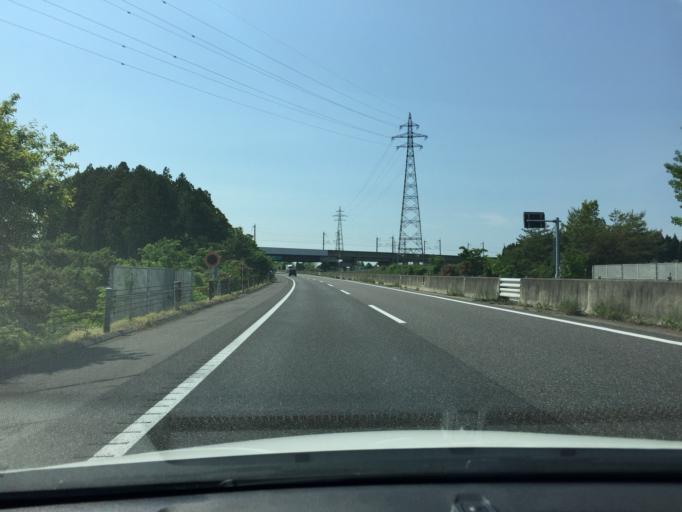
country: JP
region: Fukushima
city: Sukagawa
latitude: 37.3104
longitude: 140.3447
